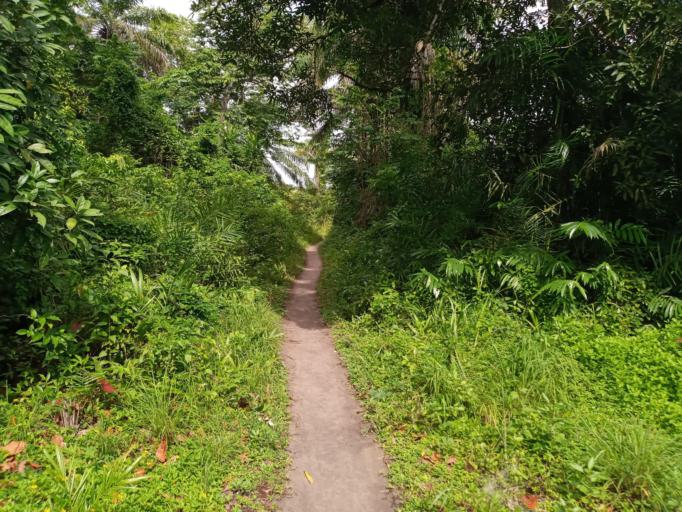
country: SL
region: Southern Province
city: Bonthe
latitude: 7.5195
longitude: -12.5386
